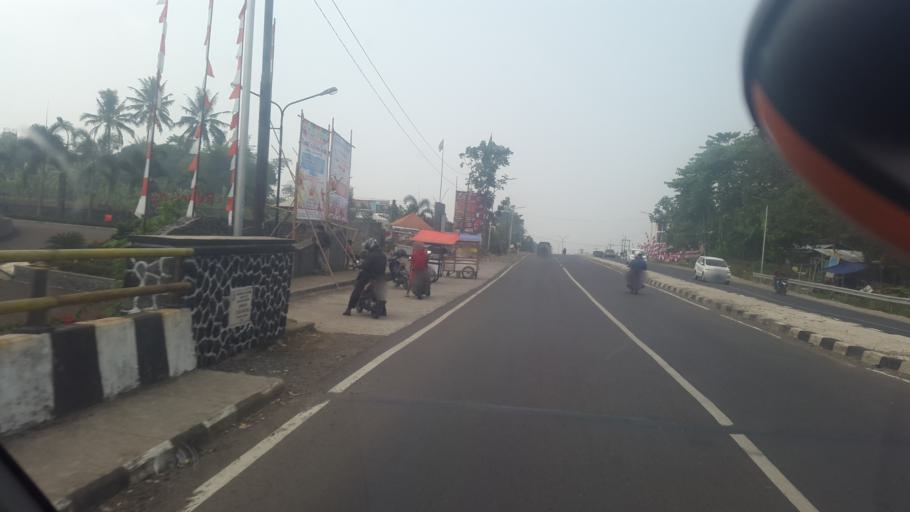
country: ID
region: West Java
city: Sukabumi
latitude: -6.9317
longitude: 106.9016
